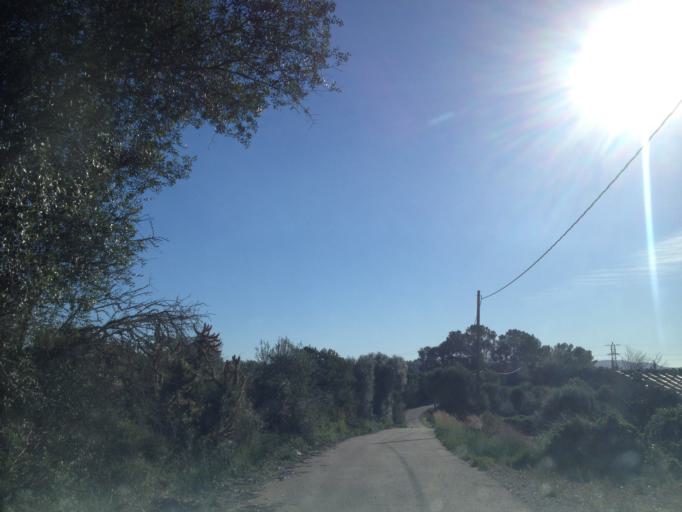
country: ES
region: Balearic Islands
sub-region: Illes Balears
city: Sineu
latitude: 39.6541
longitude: 3.0347
